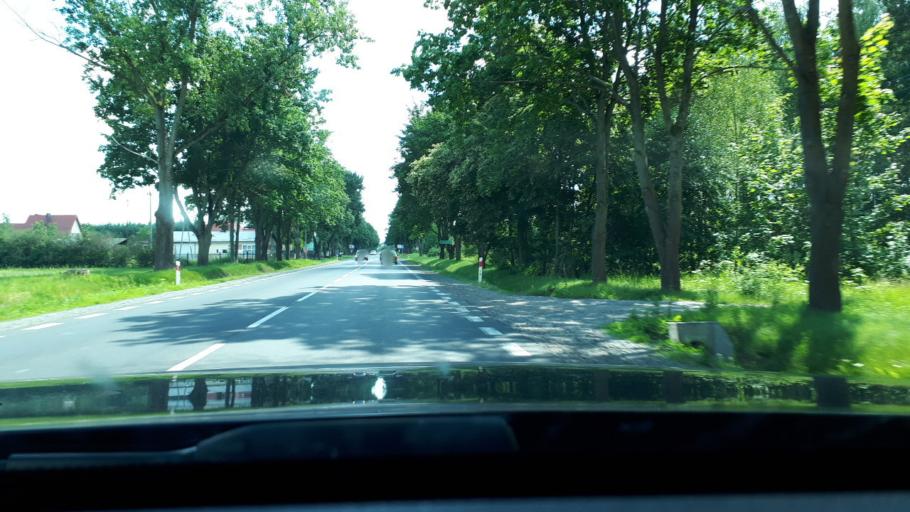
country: PL
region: Masovian Voivodeship
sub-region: Powiat piaseczynski
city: Gora Kalwaria
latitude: 51.9563
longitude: 21.2133
